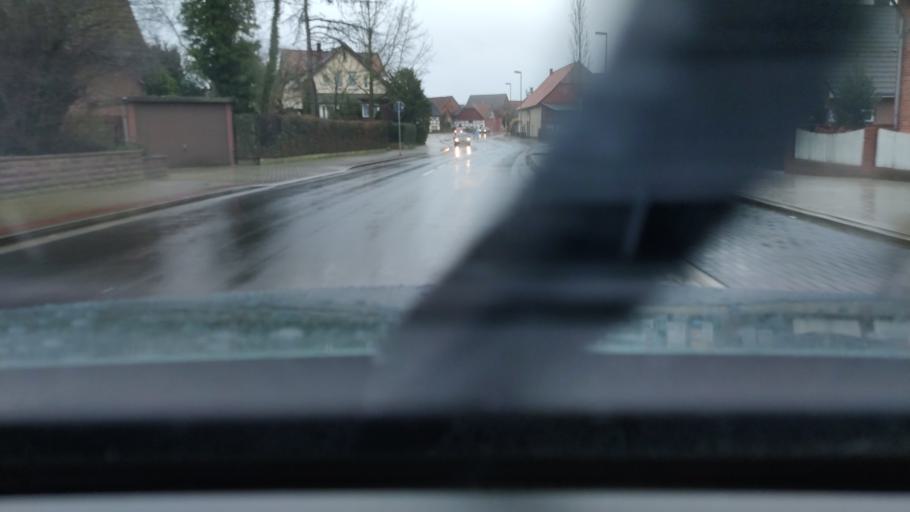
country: DE
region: Lower Saxony
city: Peine
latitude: 52.2891
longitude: 10.2320
